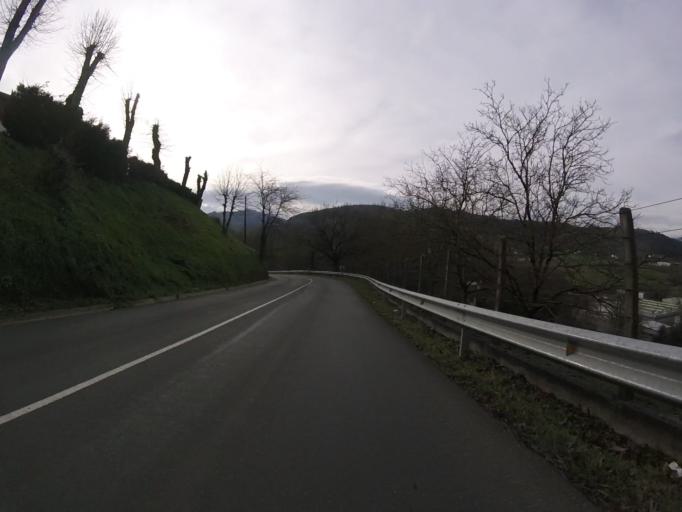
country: ES
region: Basque Country
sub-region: Provincia de Guipuzcoa
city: Azpeitia
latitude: 43.1740
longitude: -2.2492
